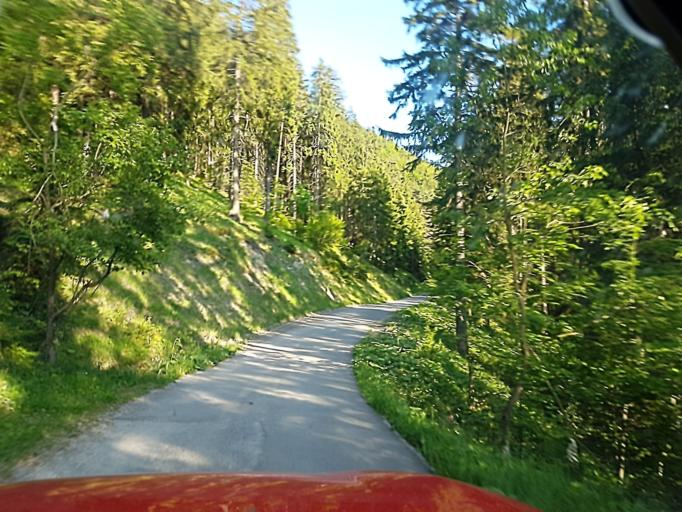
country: SK
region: Zilinsky
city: Ruzomberok
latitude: 49.0593
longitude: 19.2752
